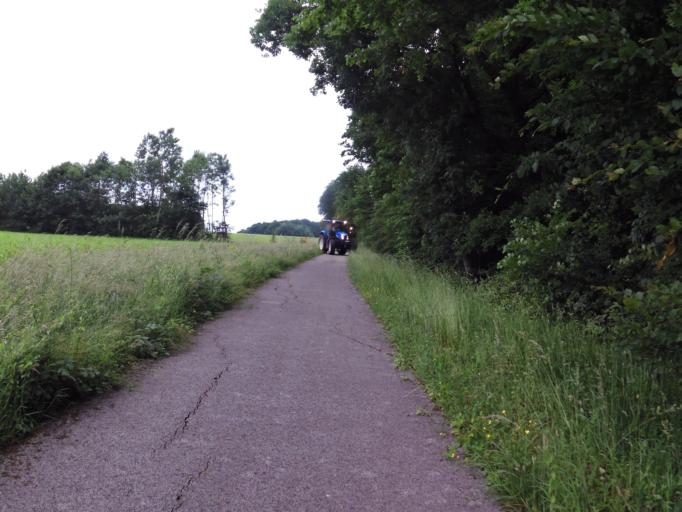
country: FR
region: Champagne-Ardenne
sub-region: Departement de la Haute-Marne
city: Montier-en-Der
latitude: 48.5406
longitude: 4.7680
